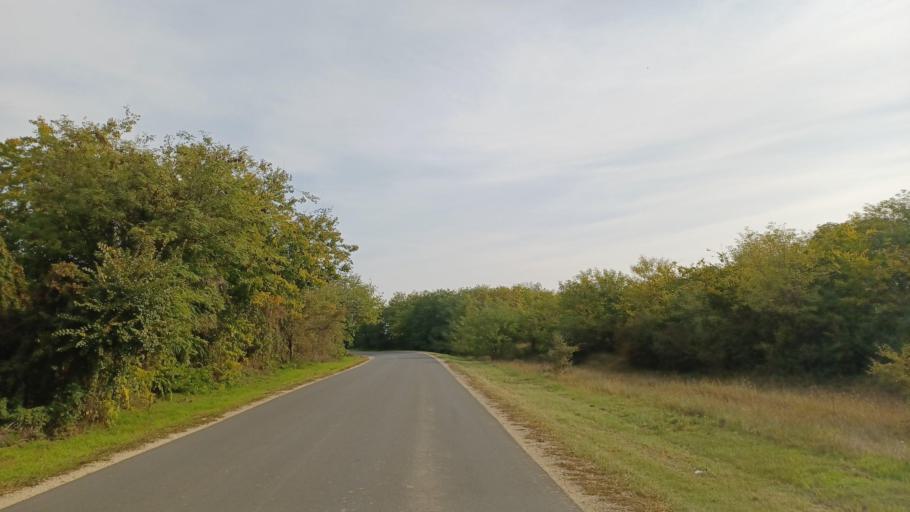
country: HU
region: Tolna
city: Nagydorog
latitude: 46.6316
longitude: 18.6671
